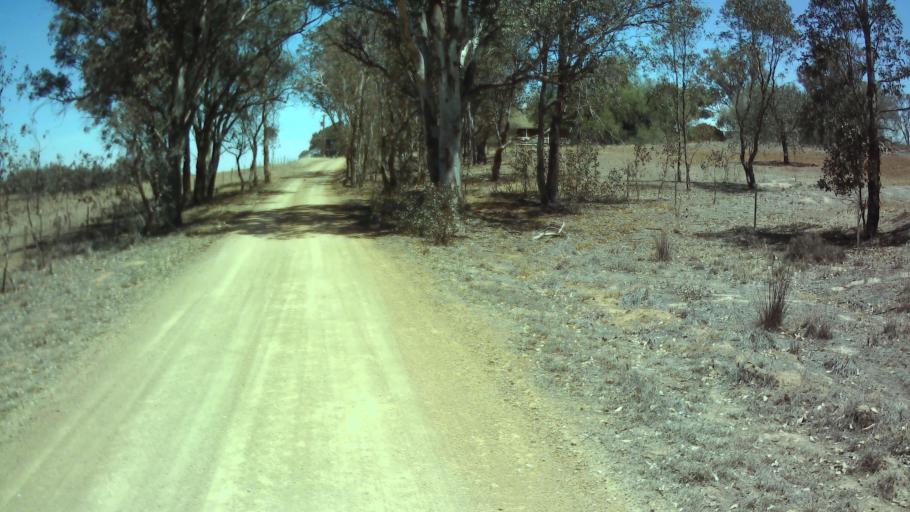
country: AU
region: New South Wales
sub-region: Weddin
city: Grenfell
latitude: -33.9298
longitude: 148.1537
